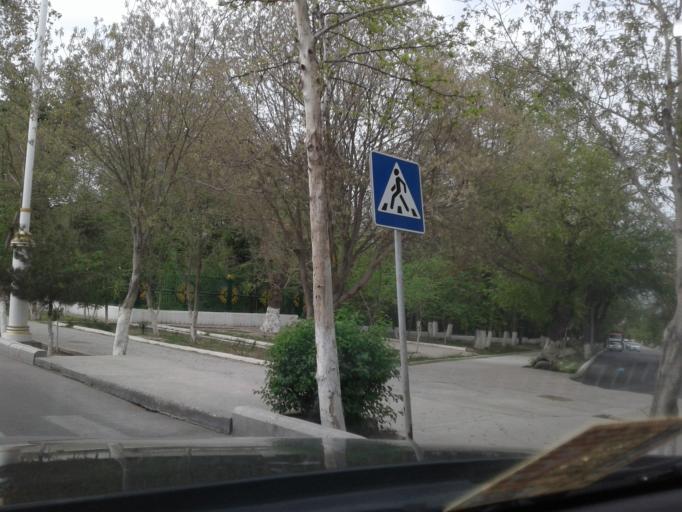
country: TM
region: Ahal
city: Ashgabat
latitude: 37.9485
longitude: 58.3487
